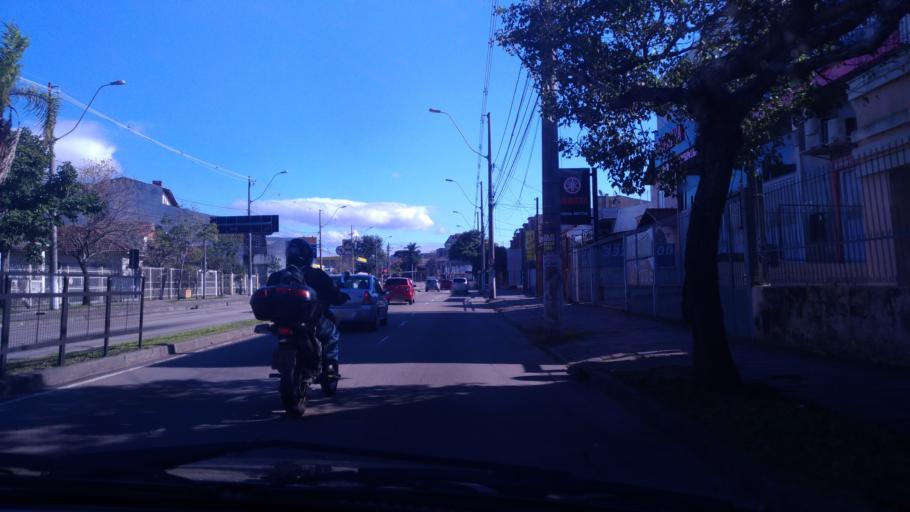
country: BR
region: Rio Grande do Sul
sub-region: Porto Alegre
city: Porto Alegre
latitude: -30.0735
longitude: -51.2004
